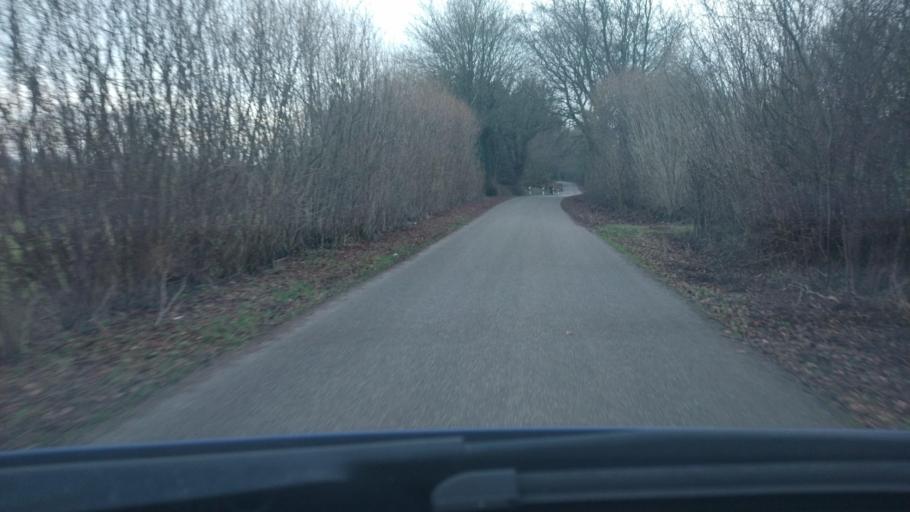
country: DE
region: Schleswig-Holstein
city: Neuberend
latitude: 54.5433
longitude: 9.5450
